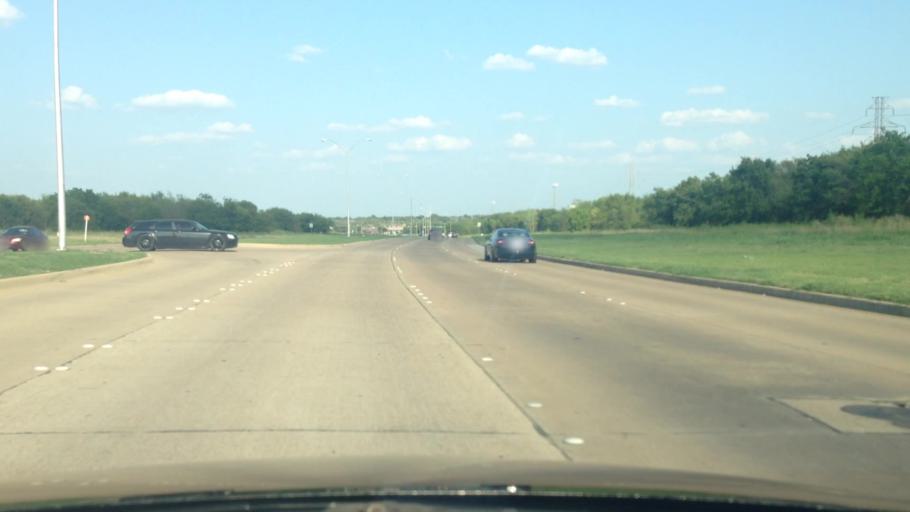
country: US
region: Texas
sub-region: Tarrant County
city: Edgecliff Village
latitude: 32.6488
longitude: -97.3470
